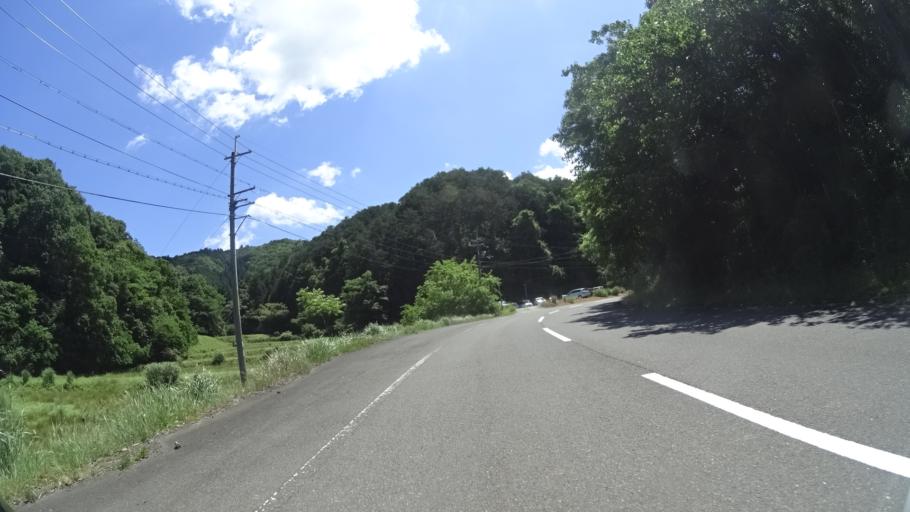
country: JP
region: Kyoto
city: Miyazu
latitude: 35.4188
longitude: 135.1681
